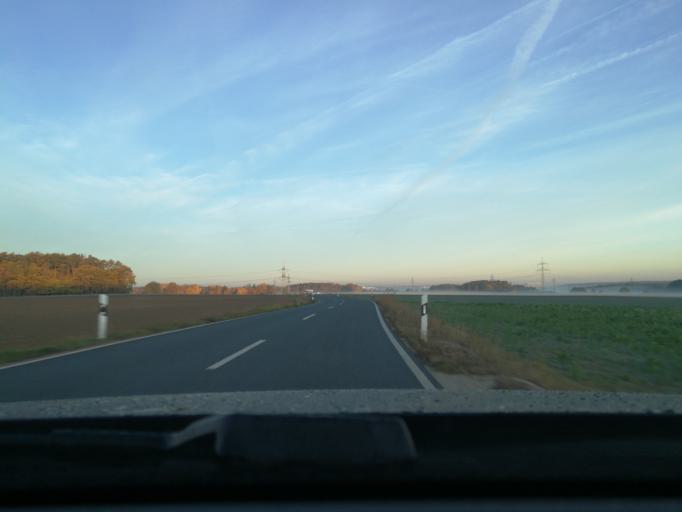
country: DE
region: Bavaria
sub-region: Regierungsbezirk Mittelfranken
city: Obermichelbach
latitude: 49.5455
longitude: 10.9302
